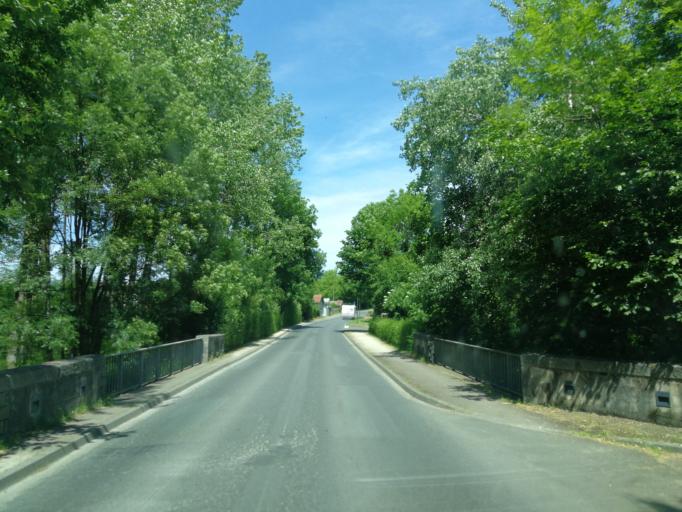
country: FR
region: Poitou-Charentes
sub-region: Departement des Deux-Sevres
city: La Foret-sur-Sevre
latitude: 46.7729
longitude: -0.6462
